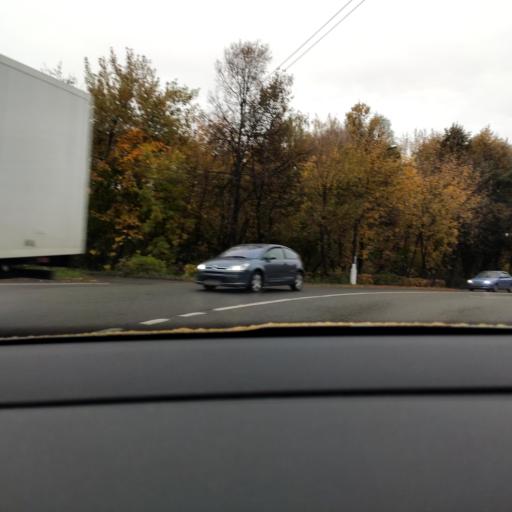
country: RU
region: Moskovskaya
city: Ivanteyevka
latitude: 55.9718
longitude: 37.9443
